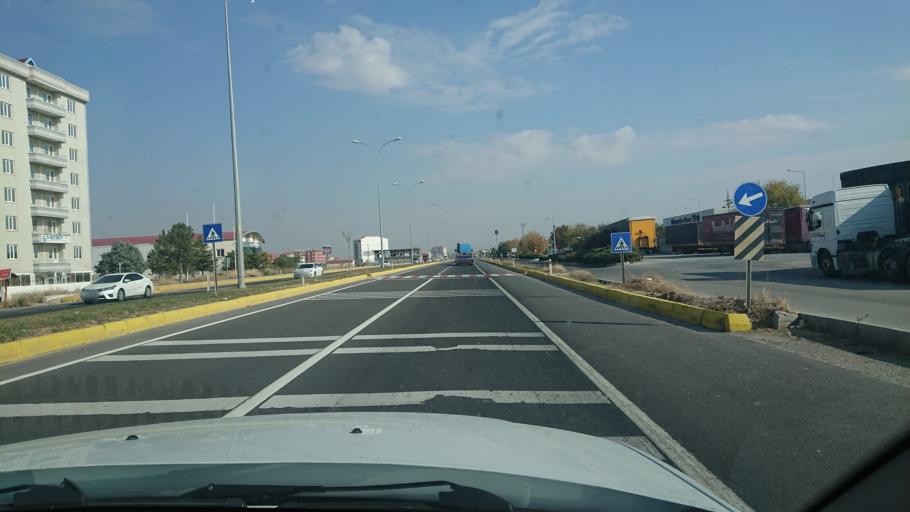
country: TR
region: Aksaray
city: Aksaray
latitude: 38.3503
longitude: 33.9623
